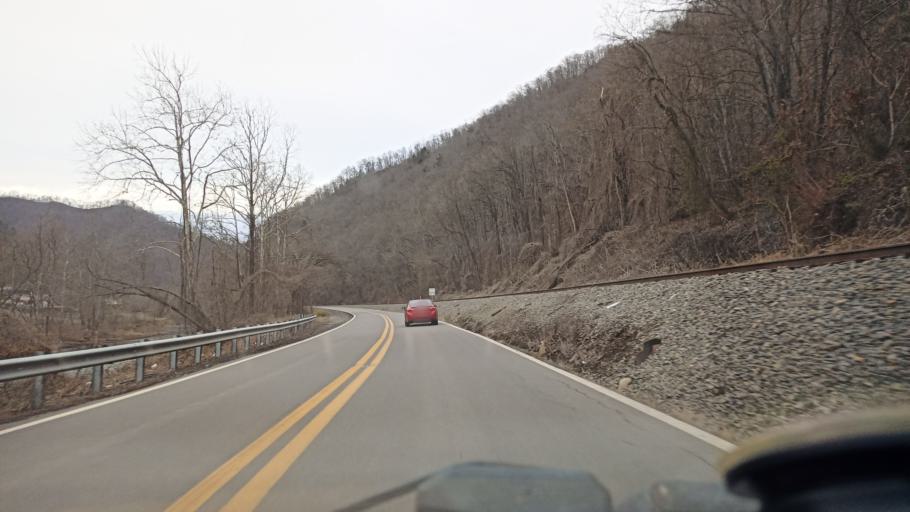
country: US
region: West Virginia
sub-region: Logan County
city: Mallory
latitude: 37.7171
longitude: -81.8680
